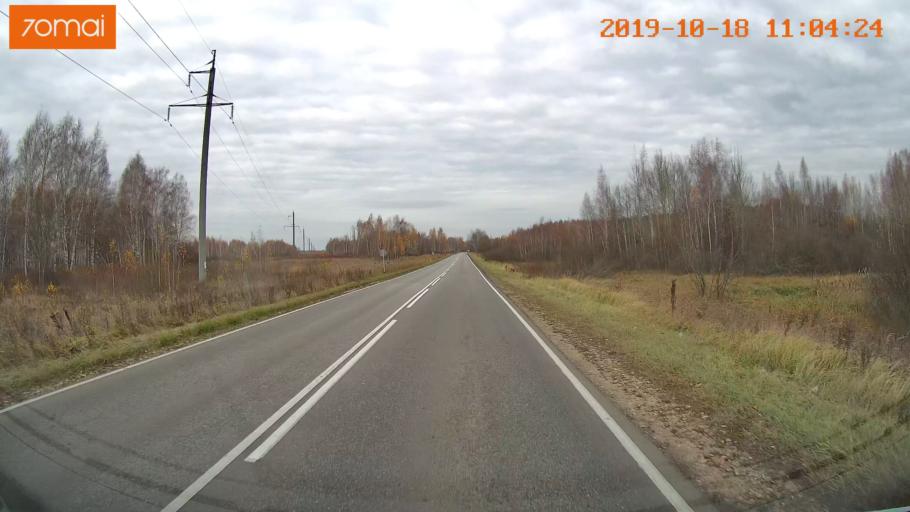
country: RU
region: Tula
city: Yepifan'
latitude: 53.8931
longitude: 38.5484
